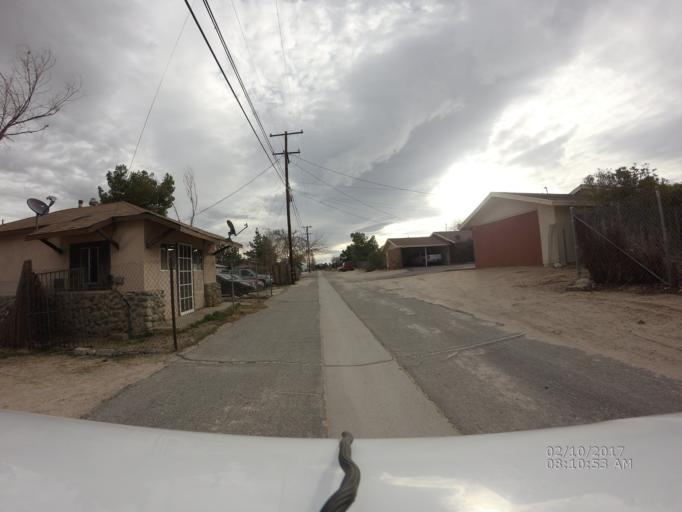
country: US
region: California
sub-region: Los Angeles County
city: Littlerock
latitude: 34.5056
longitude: -117.9067
